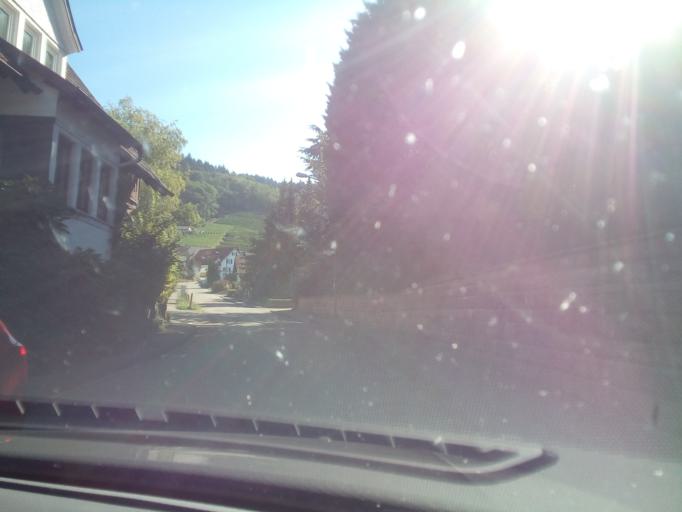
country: DE
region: Baden-Wuerttemberg
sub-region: Freiburg Region
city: Oberkirch
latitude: 48.5347
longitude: 8.0832
